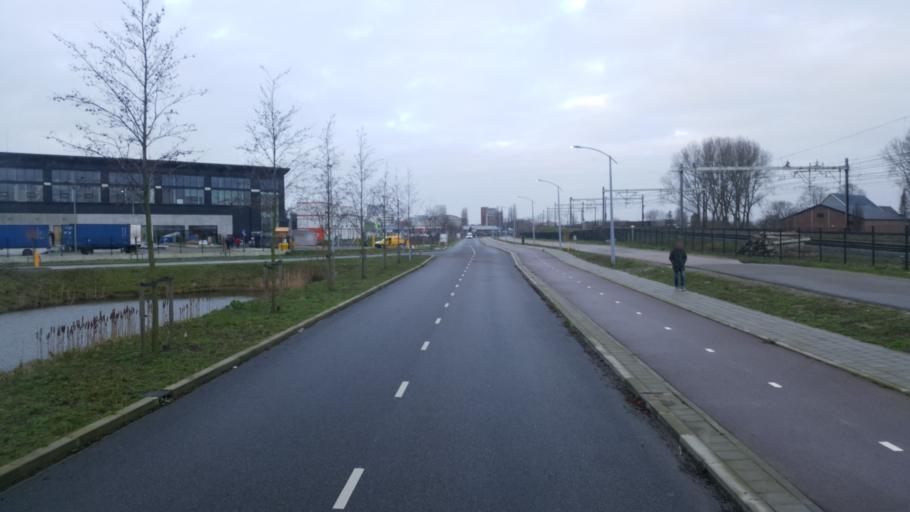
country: NL
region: North Holland
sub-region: Gemeente Haarlemmermeer
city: Hoofddorp
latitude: 52.2963
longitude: 4.7246
